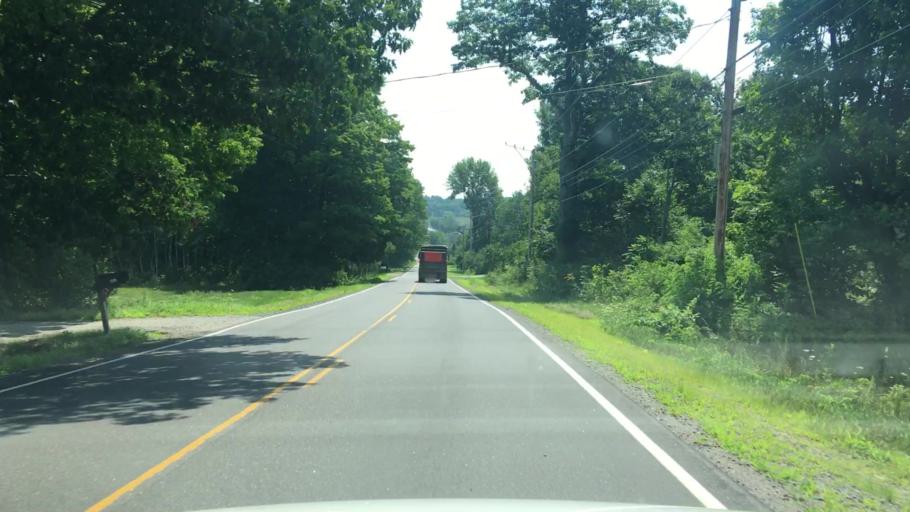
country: US
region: Maine
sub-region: Kennebec County
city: Hallowell
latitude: 44.3034
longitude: -69.8187
